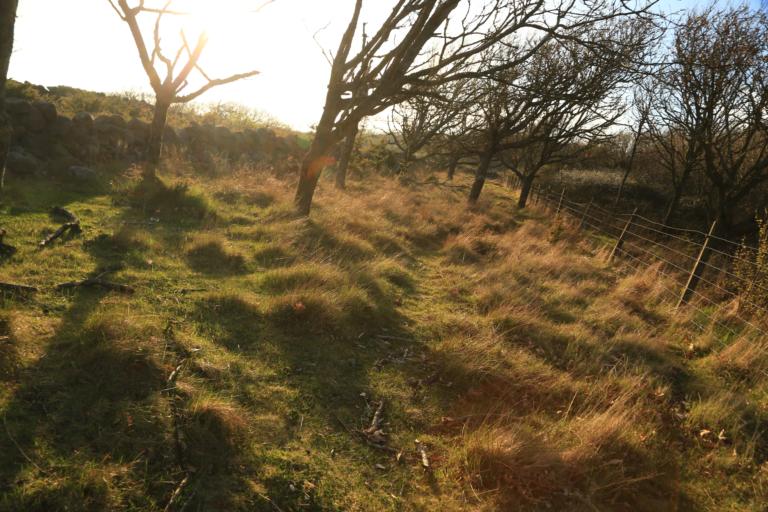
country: SE
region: Halland
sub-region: Varbergs Kommun
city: Traslovslage
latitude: 57.0386
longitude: 12.2964
